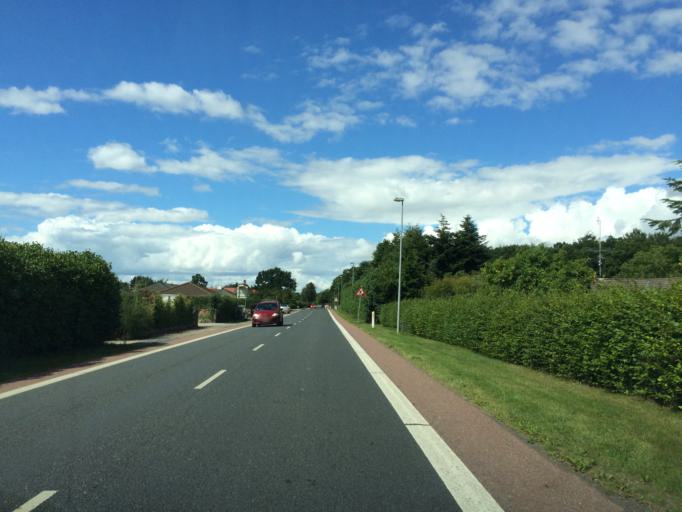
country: DK
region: South Denmark
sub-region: Assens Kommune
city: Harby
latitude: 55.1439
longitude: 10.1589
